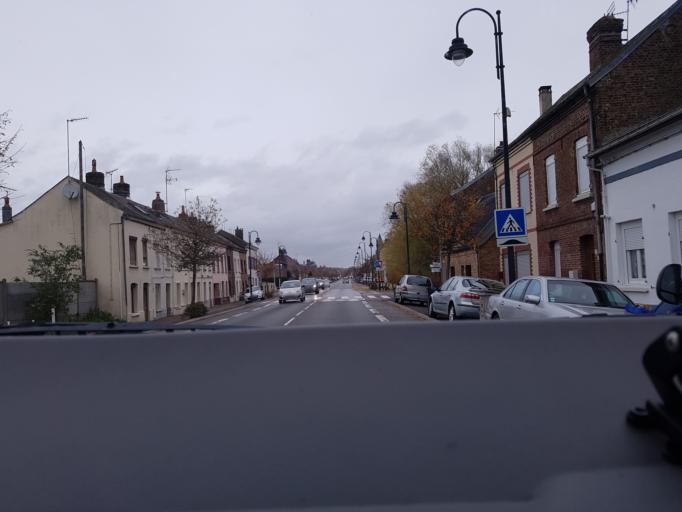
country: FR
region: Picardie
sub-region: Departement de la Somme
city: Abbeville
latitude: 50.1068
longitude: 1.8022
